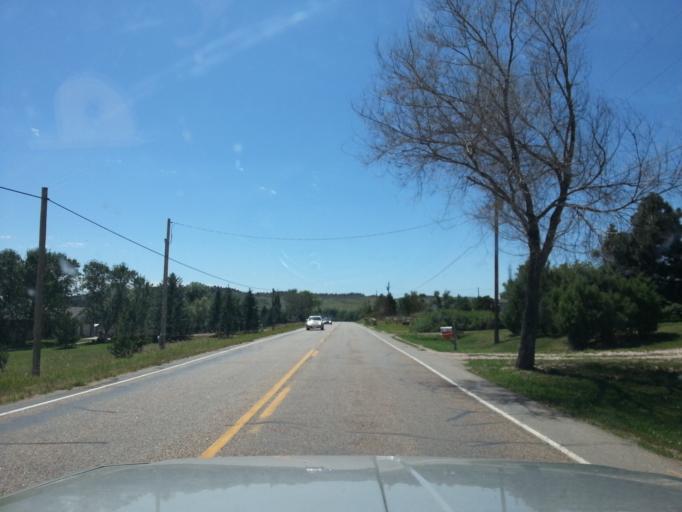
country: US
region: Colorado
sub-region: Larimer County
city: Loveland
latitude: 40.4245
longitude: -105.1922
